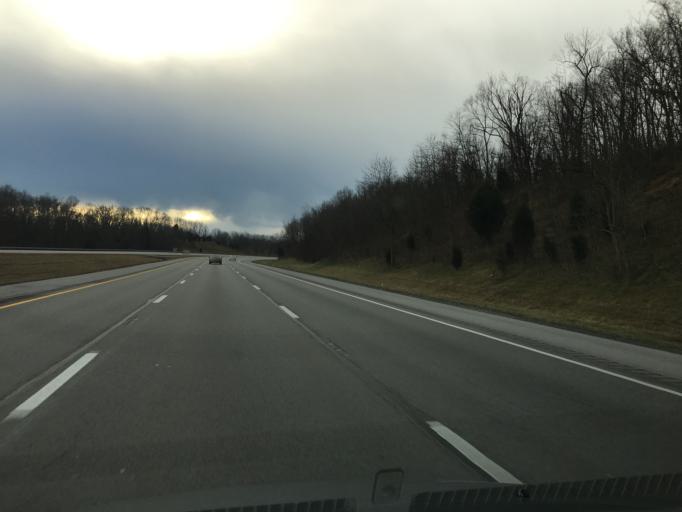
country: US
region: Kentucky
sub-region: Scott County
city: Georgetown
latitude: 38.3246
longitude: -84.5612
